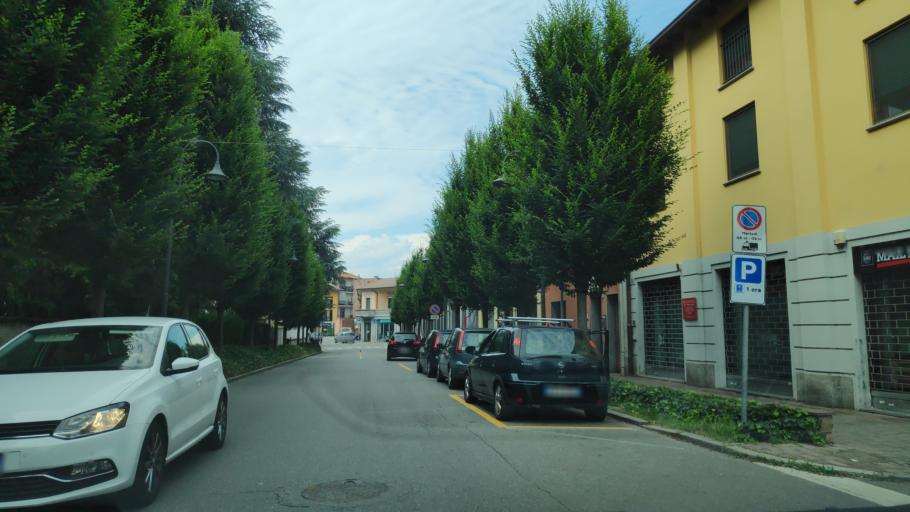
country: IT
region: Lombardy
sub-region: Citta metropolitana di Milano
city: Melzo
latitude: 45.4954
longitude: 9.4232
